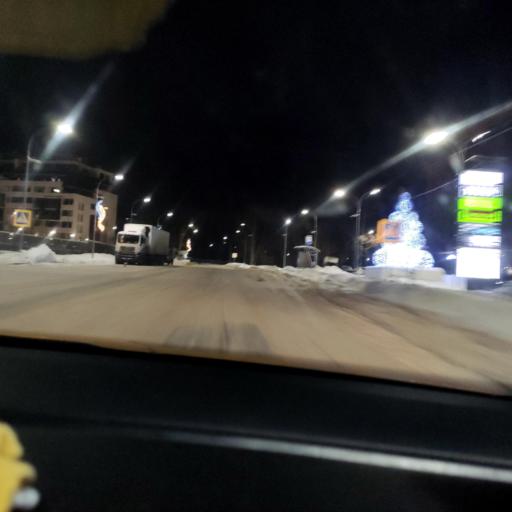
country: RU
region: Moskovskaya
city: Krasnogorsk
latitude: 55.8765
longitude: 37.3137
